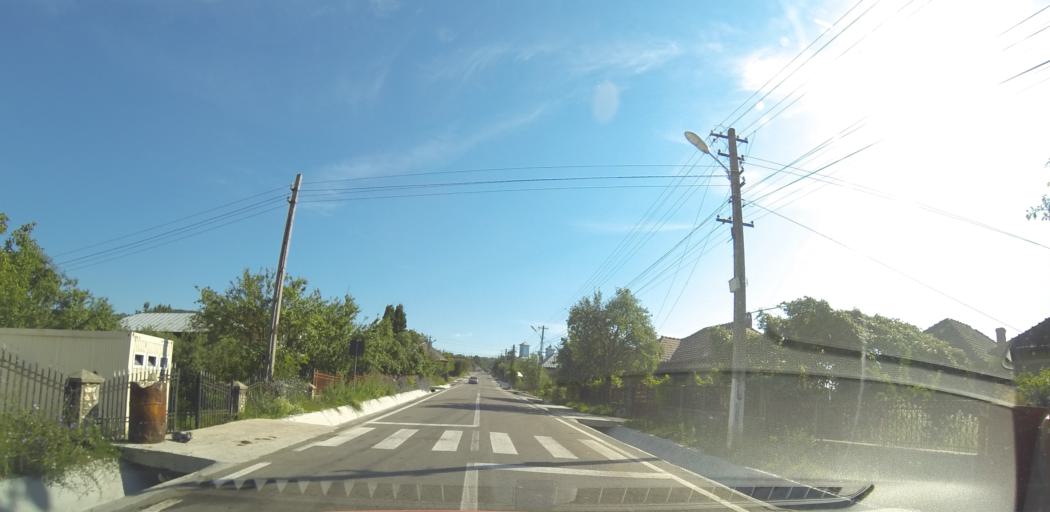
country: RO
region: Valcea
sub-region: Comuna Vaideeni
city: Vaideeni
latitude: 45.1649
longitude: 23.8975
